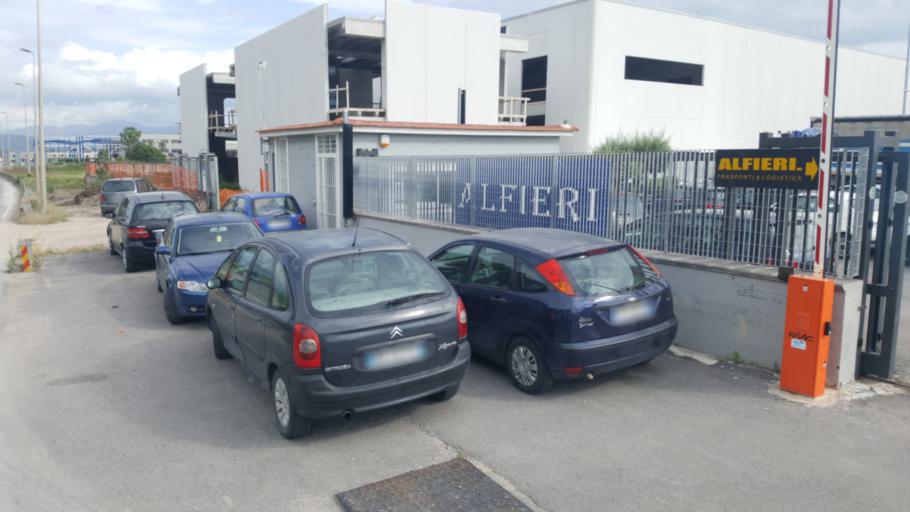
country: IT
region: Campania
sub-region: Provincia di Caserta
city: San Felice A Cancello
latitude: 40.9777
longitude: 14.4717
